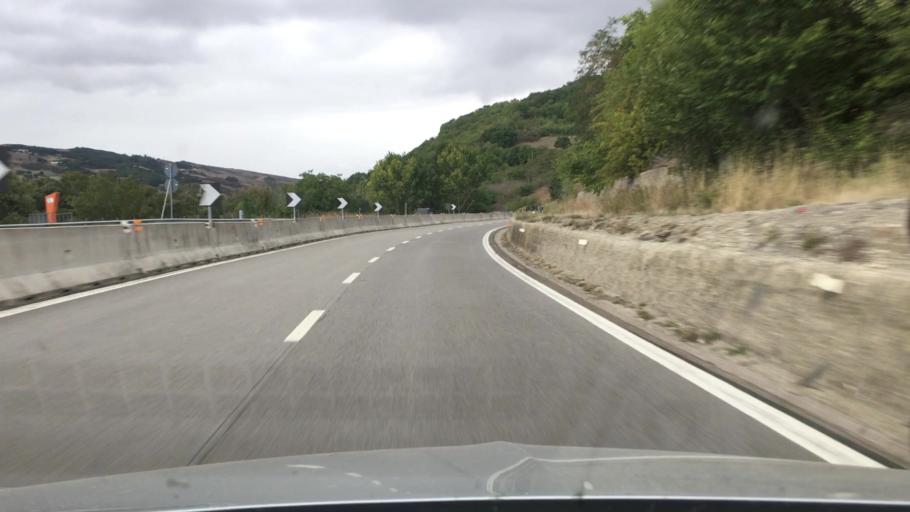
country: IT
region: Basilicate
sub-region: Provincia di Potenza
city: Vaglio Basilicata
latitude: 40.6521
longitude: 15.9220
